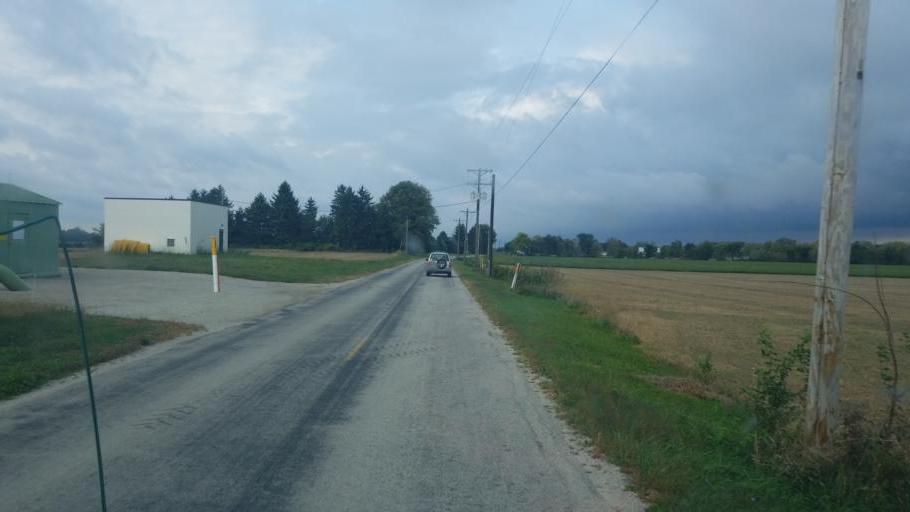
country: US
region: Ohio
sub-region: Wood County
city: North Baltimore
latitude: 41.1836
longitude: -83.6208
